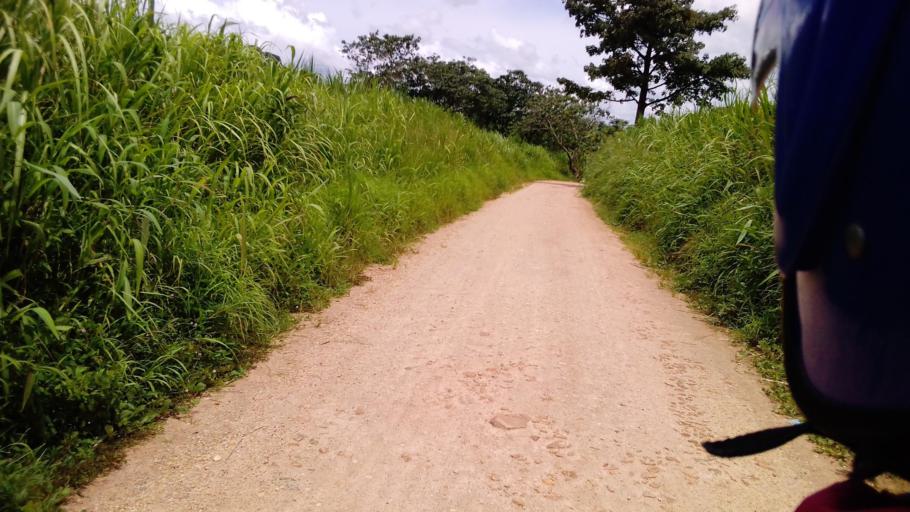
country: SL
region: Eastern Province
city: Koidu
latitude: 8.6681
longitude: -10.9450
